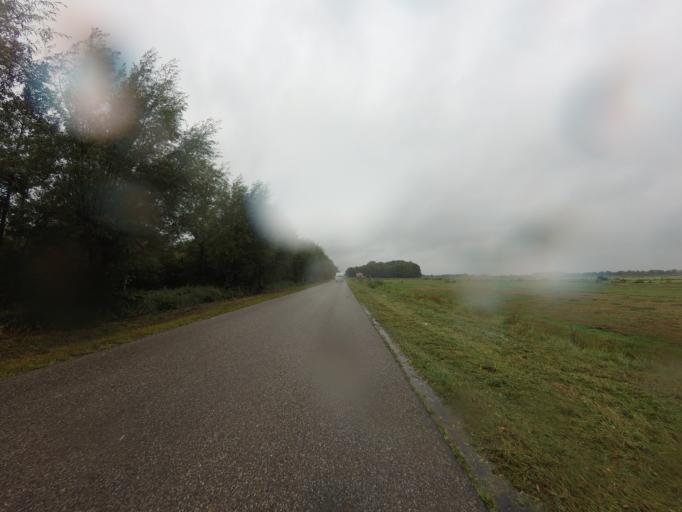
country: NL
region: Friesland
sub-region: Gemeente Tytsjerksteradiel
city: Garyp
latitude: 53.1333
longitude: 5.9563
